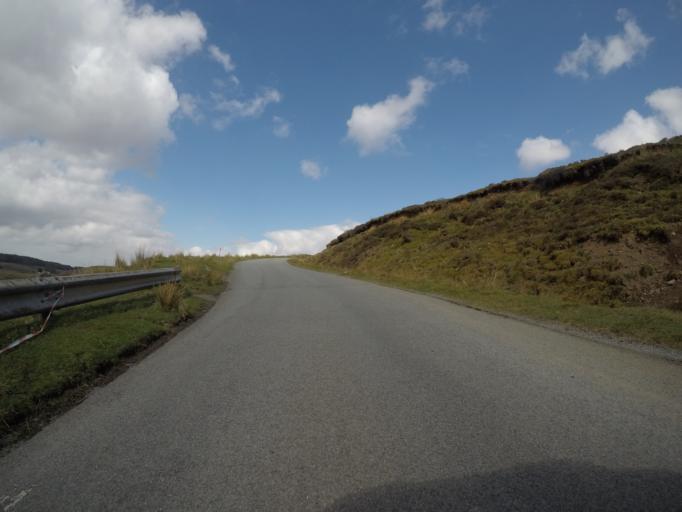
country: GB
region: Scotland
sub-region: Highland
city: Isle of Skye
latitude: 57.4153
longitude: -6.2960
